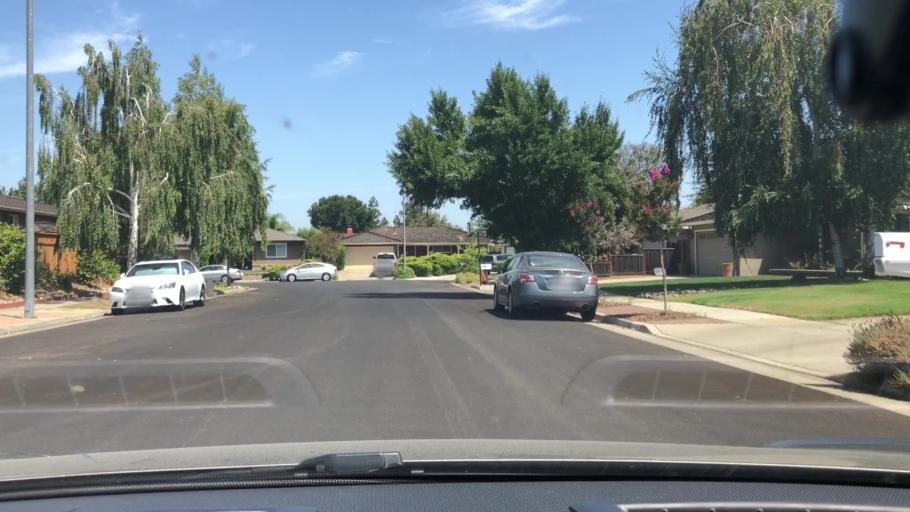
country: US
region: California
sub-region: Santa Clara County
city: Monte Sereno
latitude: 37.2645
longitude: -121.9895
